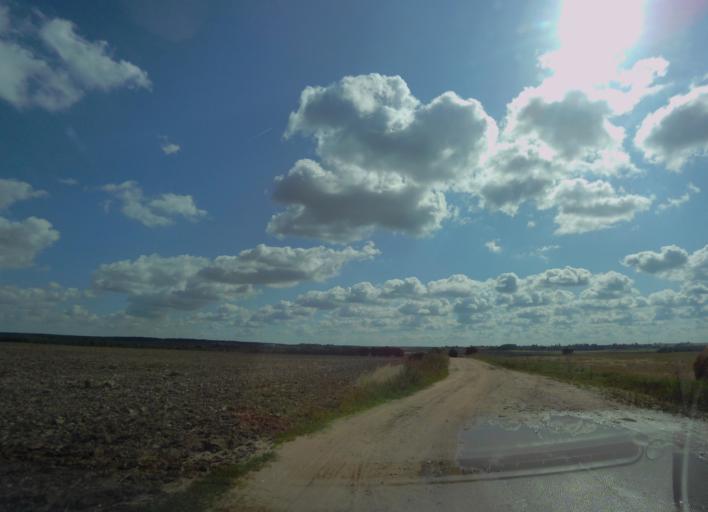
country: BY
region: Minsk
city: Zyembin
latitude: 54.3796
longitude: 28.3492
